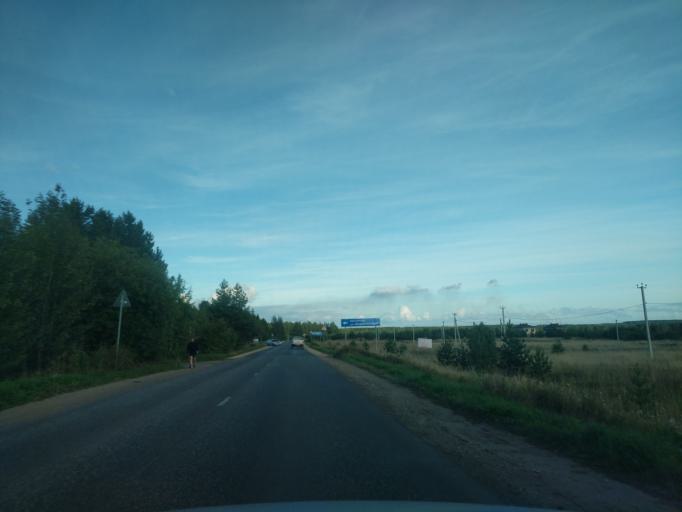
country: RU
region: Kirov
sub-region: Kirovo-Chepetskiy Rayon
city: Kirov
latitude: 58.6022
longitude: 49.8244
